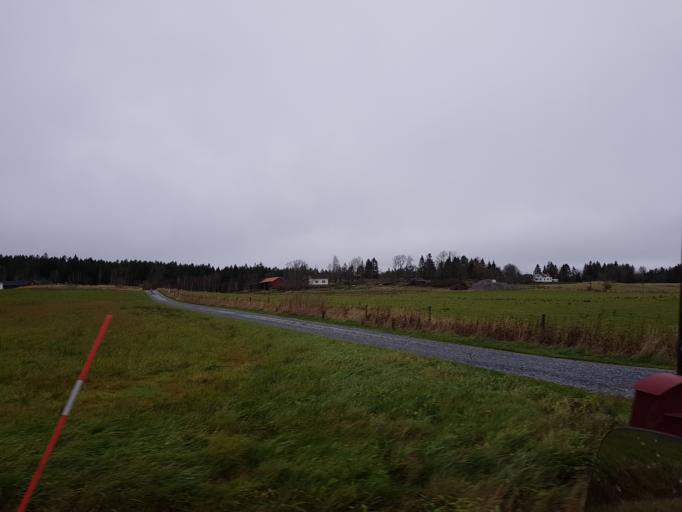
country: SE
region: Vaestra Goetaland
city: Svanesund
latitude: 58.1763
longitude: 11.7538
